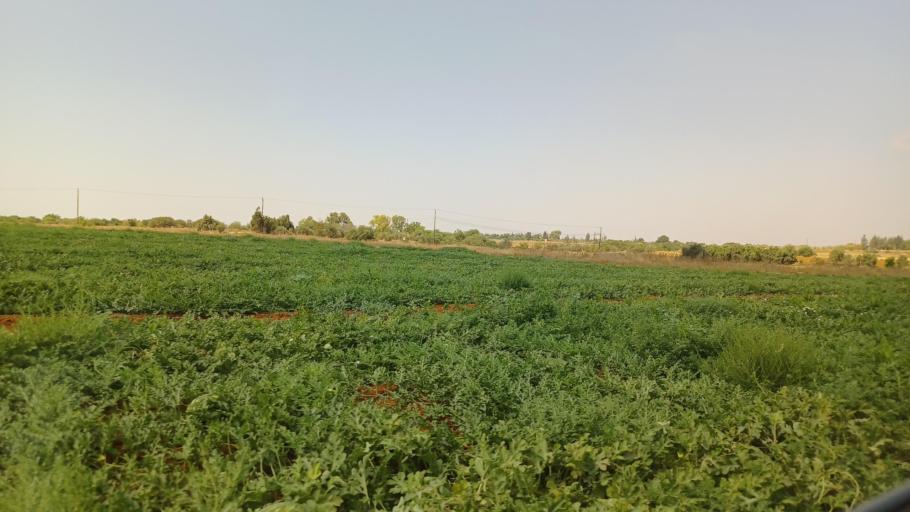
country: CY
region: Ammochostos
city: Frenaros
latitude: 35.0611
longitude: 33.9209
